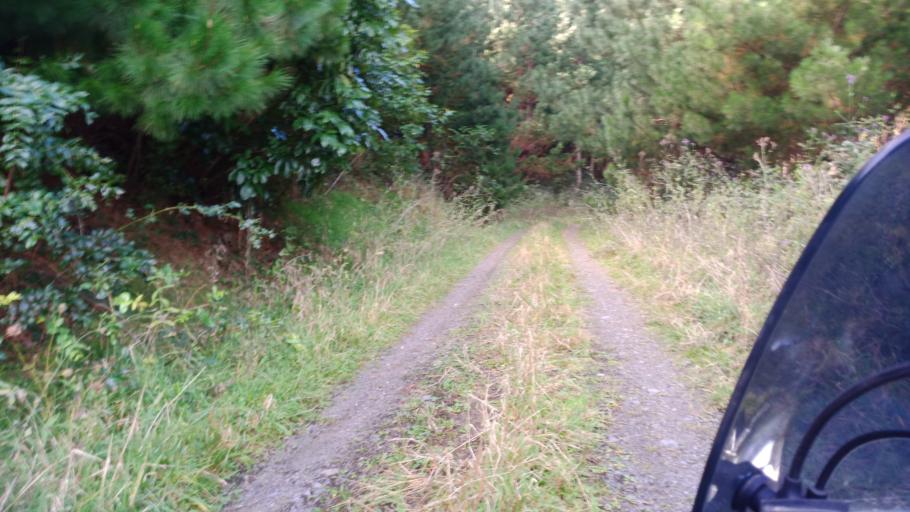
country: NZ
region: Hawke's Bay
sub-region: Wairoa District
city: Wairoa
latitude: -39.0049
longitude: 177.0796
